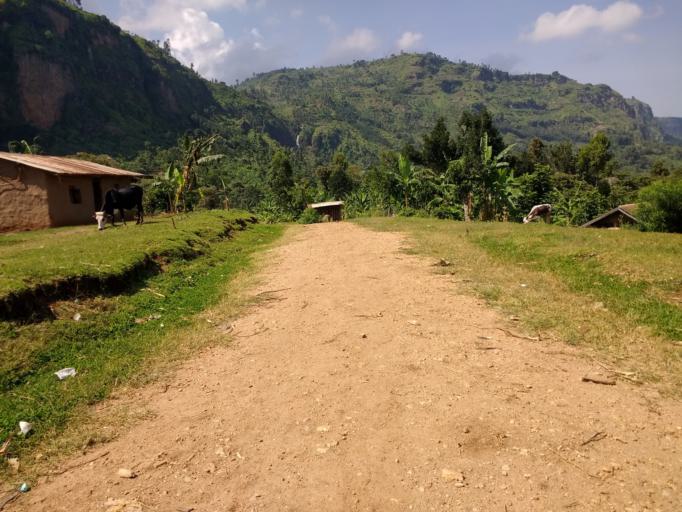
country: UG
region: Eastern Region
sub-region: Mbale District
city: Mbale
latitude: 1.0719
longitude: 34.2374
